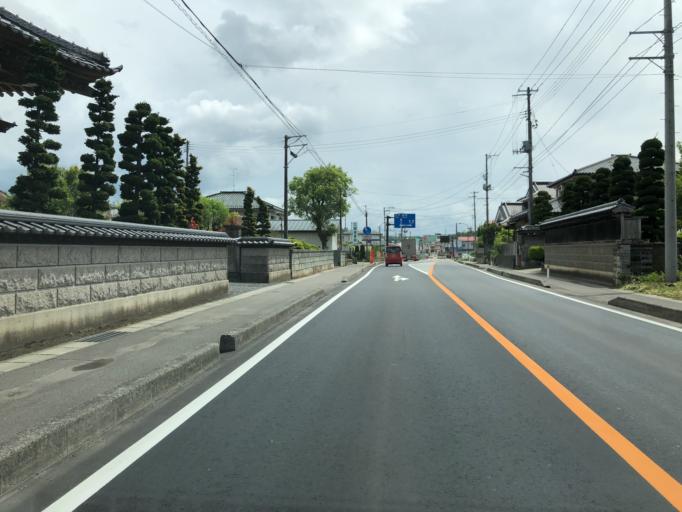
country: JP
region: Fukushima
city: Ishikawa
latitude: 37.1041
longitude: 140.3481
